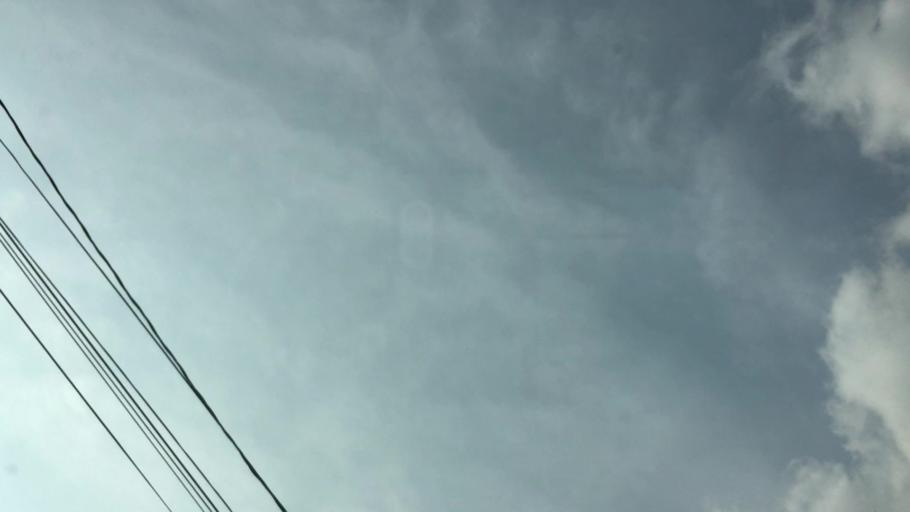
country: US
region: Alabama
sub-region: Bibb County
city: Woodstock
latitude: 33.2250
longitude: -87.1263
